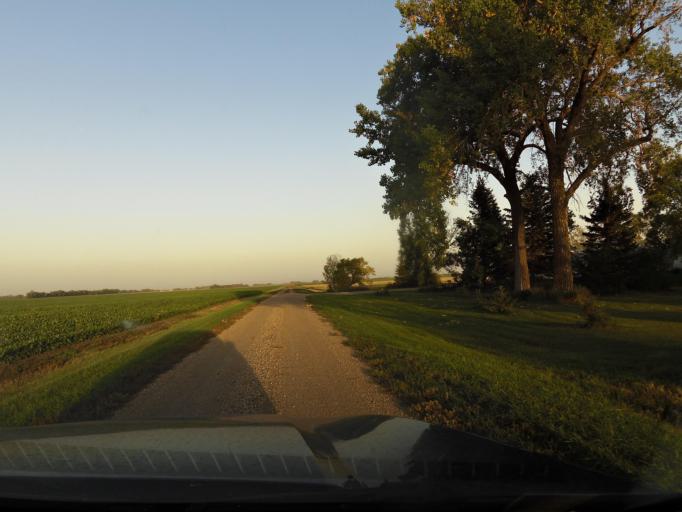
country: US
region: North Dakota
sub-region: Walsh County
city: Grafton
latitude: 48.3831
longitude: -97.2539
